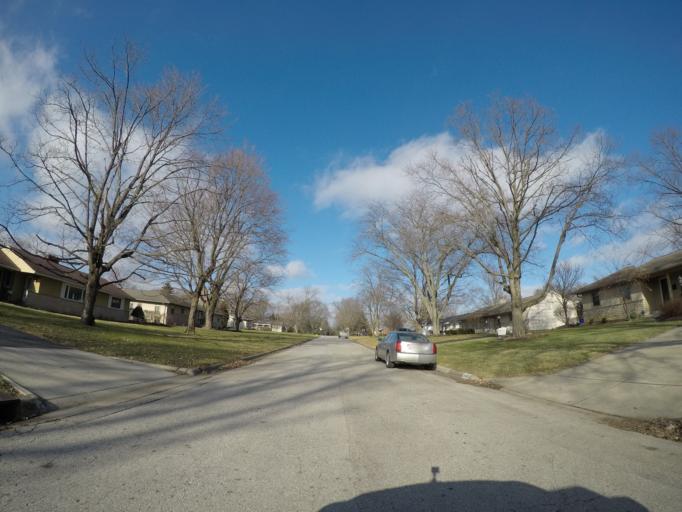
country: US
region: Ohio
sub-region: Franklin County
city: Upper Arlington
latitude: 40.0257
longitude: -83.0665
